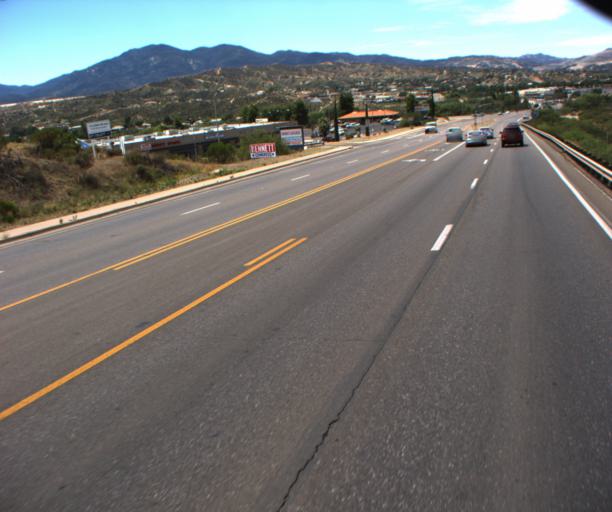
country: US
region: Arizona
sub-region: Gila County
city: Central Heights-Midland City
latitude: 33.4179
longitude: -110.8254
